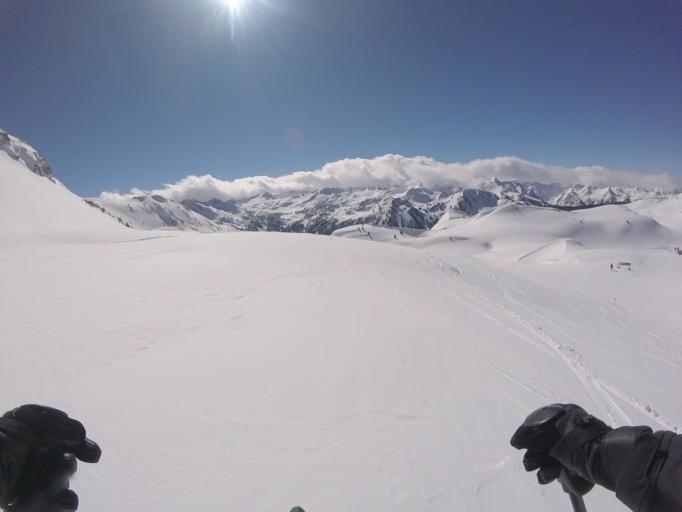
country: ES
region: Catalonia
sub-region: Provincia de Lleida
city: Espot
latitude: 42.6756
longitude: 0.9900
